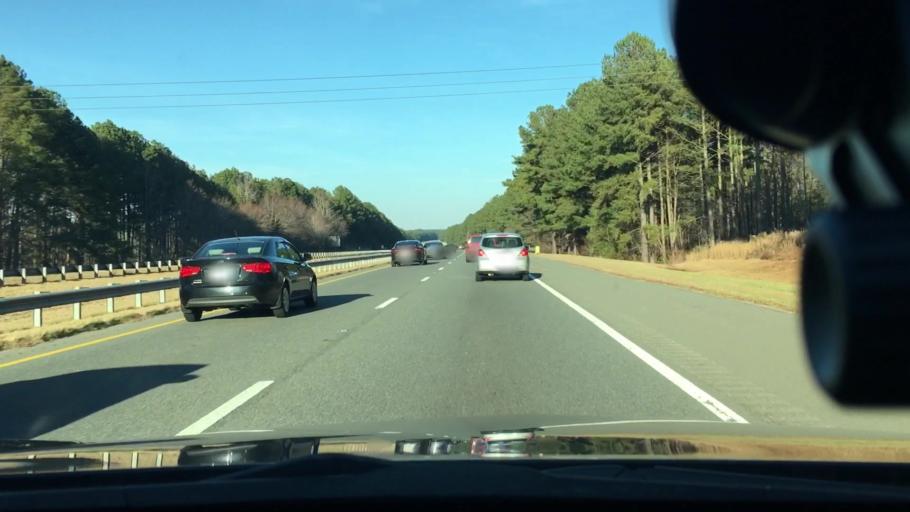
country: US
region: North Carolina
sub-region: Chatham County
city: Farmville
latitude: 35.5497
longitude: -79.1630
